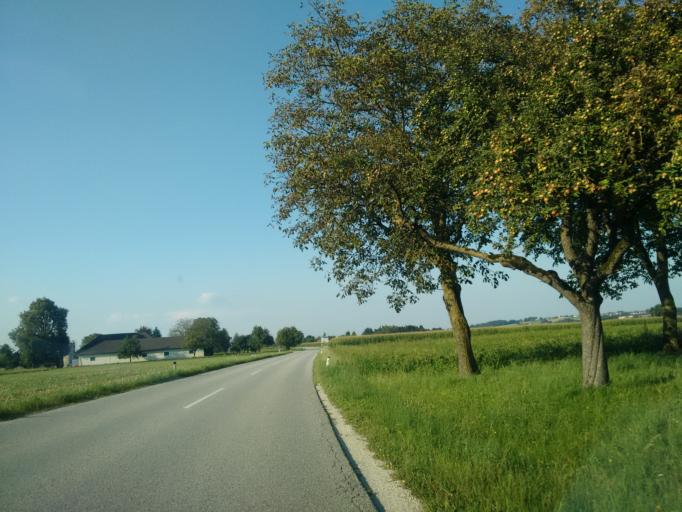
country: AT
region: Upper Austria
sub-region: Wels-Land
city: Sattledt
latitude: 47.9894
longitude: 14.0257
